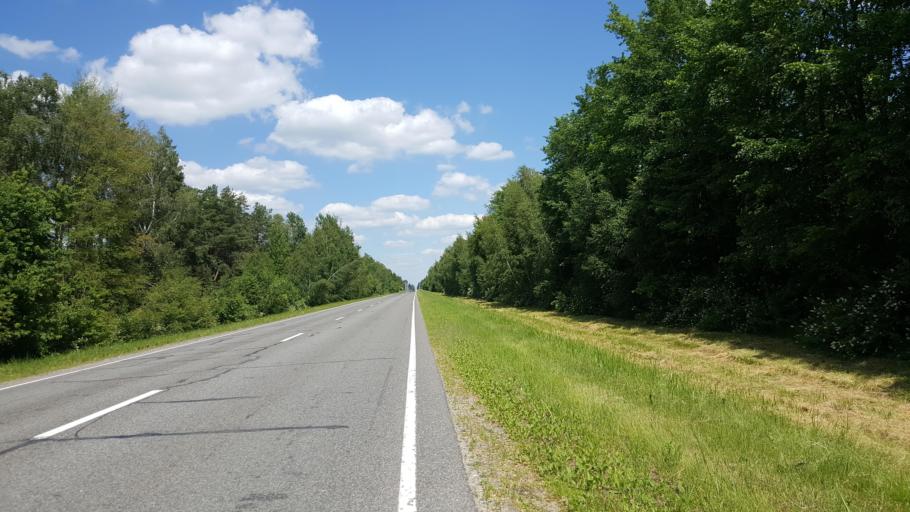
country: BY
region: Brest
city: Kamyanyets
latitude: 52.4379
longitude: 23.7852
